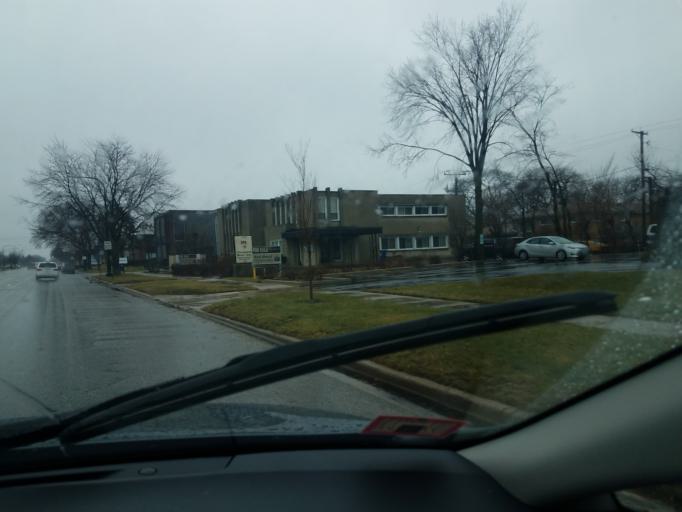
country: US
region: Illinois
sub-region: Cook County
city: Lincolnwood
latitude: 42.0152
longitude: -87.7479
